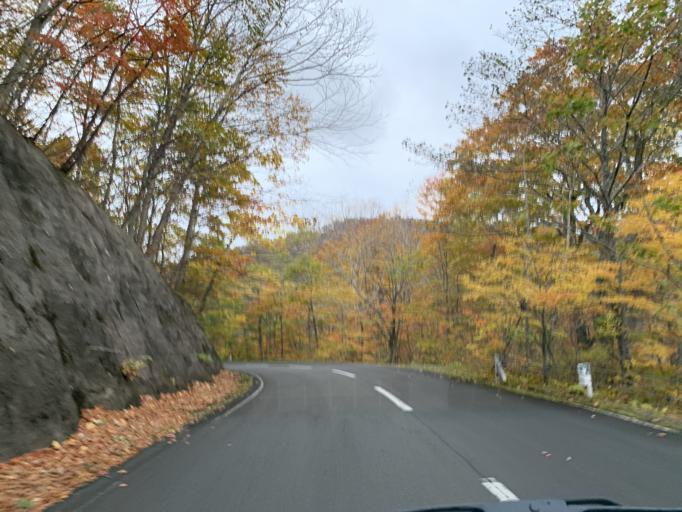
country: JP
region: Iwate
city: Mizusawa
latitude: 39.1108
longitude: 140.8559
